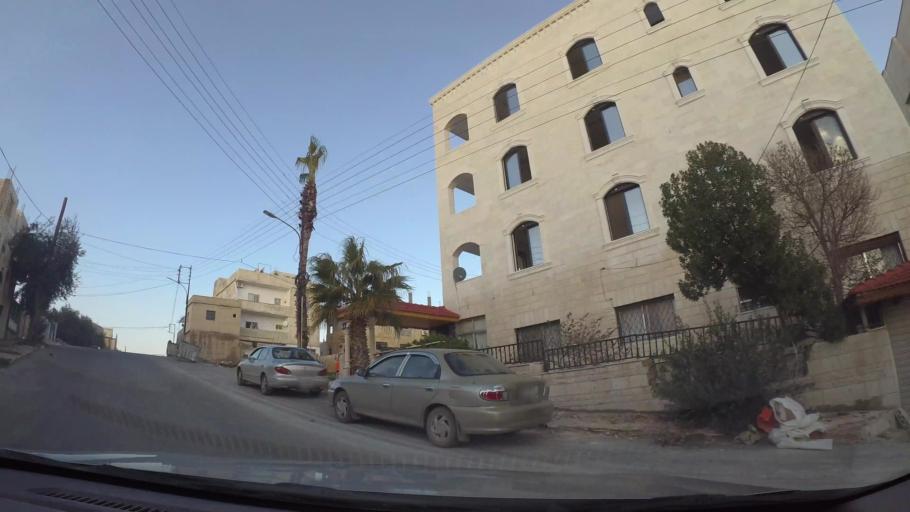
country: JO
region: Amman
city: Al Bunayyat ash Shamaliyah
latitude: 31.9042
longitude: 35.9056
